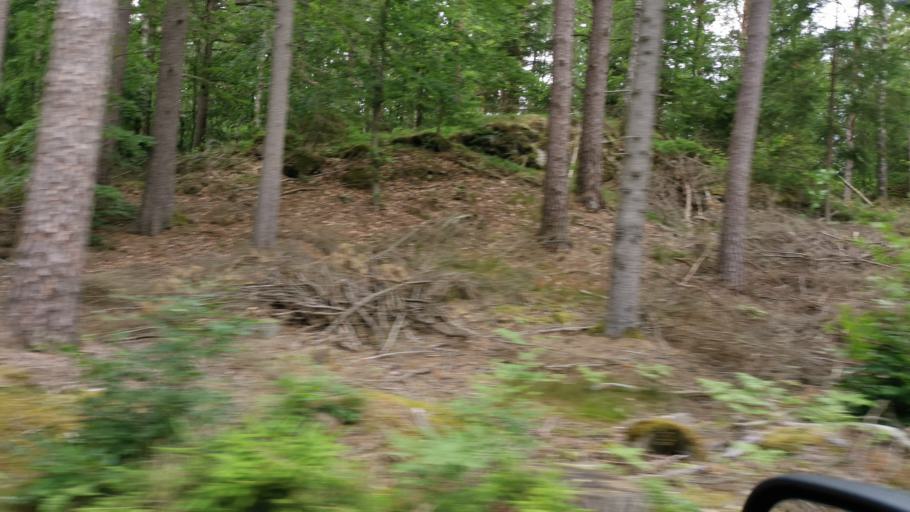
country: SE
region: Vaestra Goetaland
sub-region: Orust
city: Henan
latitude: 58.2930
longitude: 11.6041
